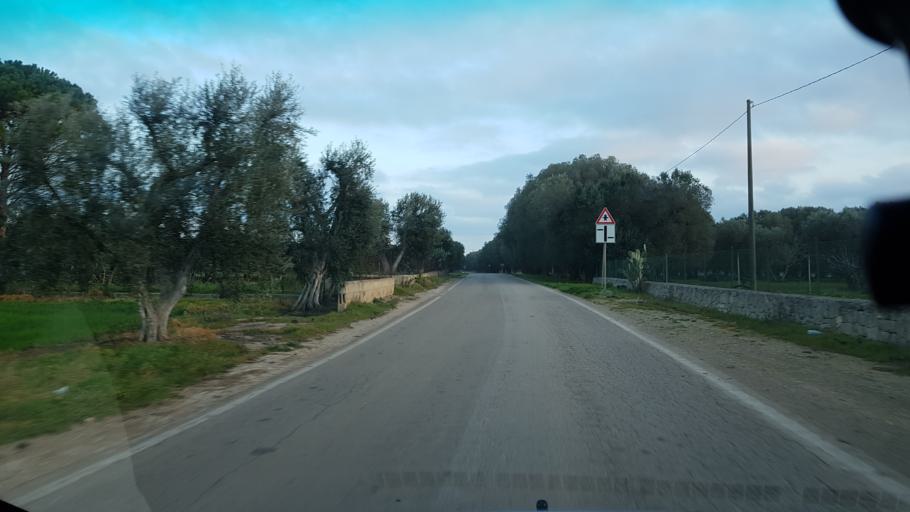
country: IT
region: Apulia
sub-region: Provincia di Brindisi
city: Mesagne
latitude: 40.6131
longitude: 17.7871
